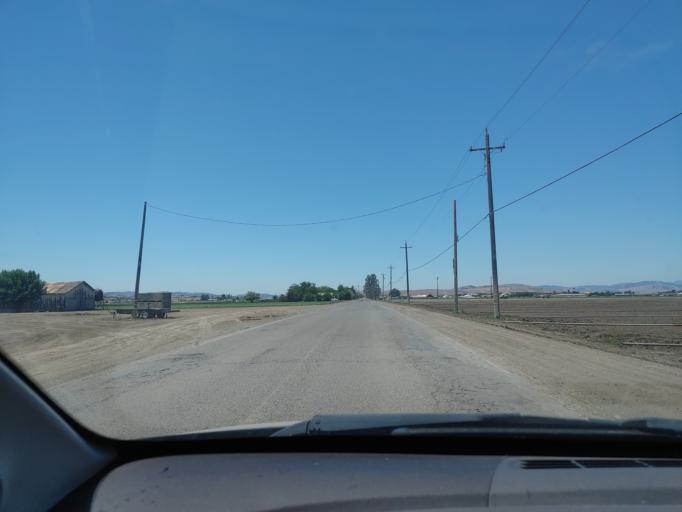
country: US
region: California
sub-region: San Benito County
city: Hollister
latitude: 36.8687
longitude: -121.3848
